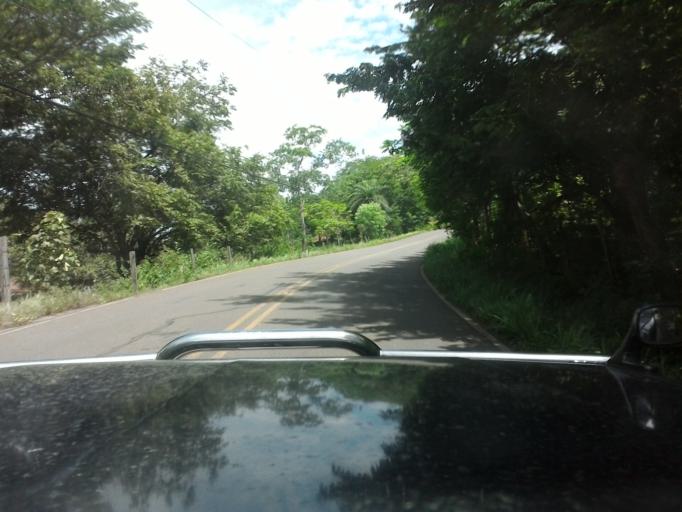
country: CR
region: Puntarenas
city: Miramar
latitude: 10.1332
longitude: -84.8403
